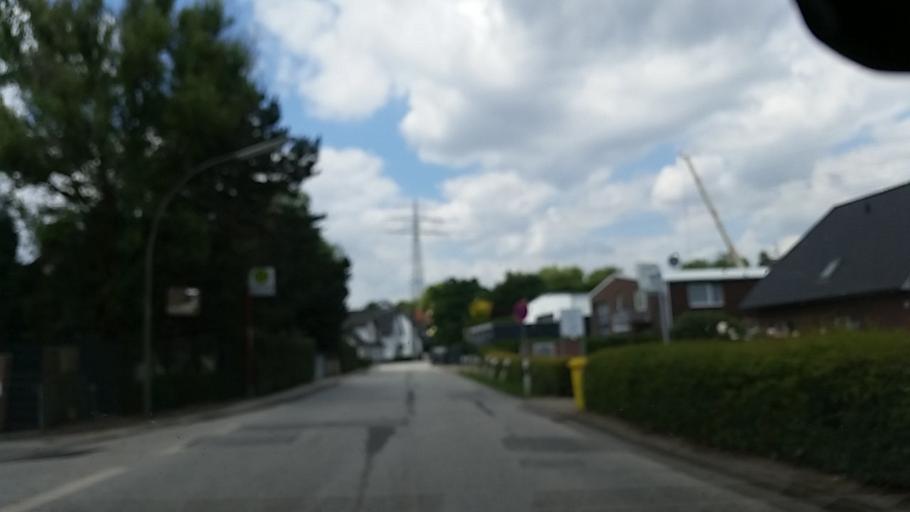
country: DE
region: Hamburg
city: Wandsbek
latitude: 53.5230
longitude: 10.1131
